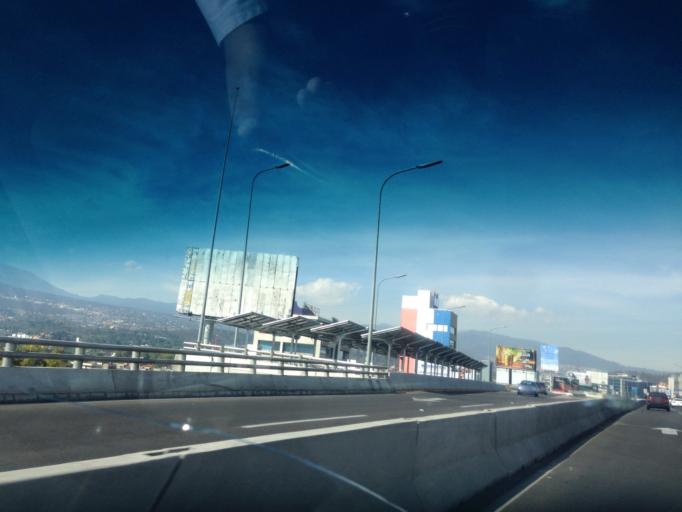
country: MX
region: Mexico City
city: Tlalpan
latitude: 19.3026
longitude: -99.1721
